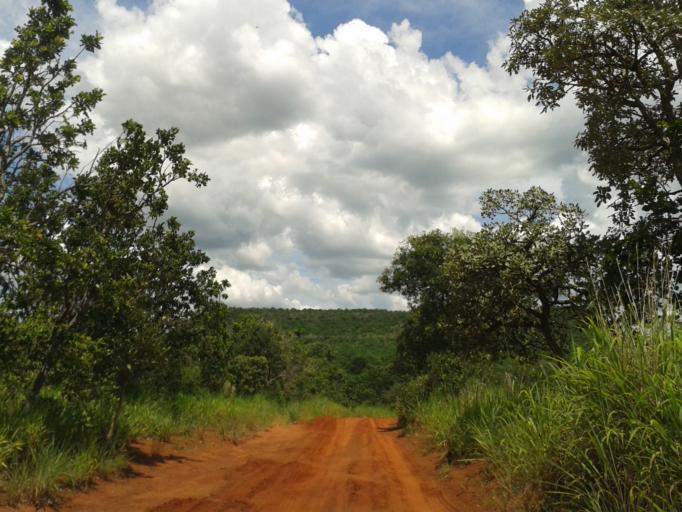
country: BR
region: Minas Gerais
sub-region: Ituiutaba
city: Ituiutaba
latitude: -18.8486
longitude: -49.5023
